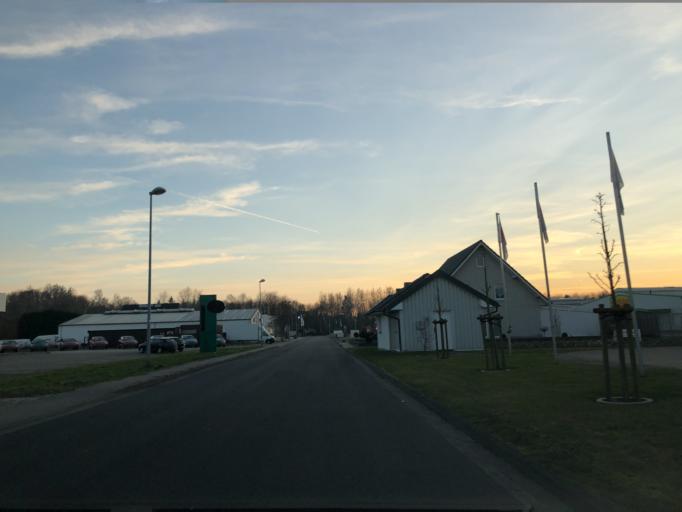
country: DE
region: Lower Saxony
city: Papenburg
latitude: 53.0931
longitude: 7.4044
